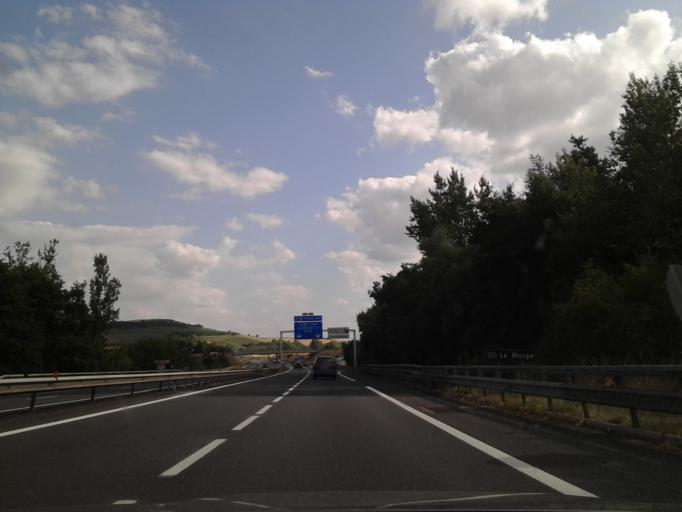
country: FR
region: Auvergne
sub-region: Departement du Puy-de-Dome
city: Combronde
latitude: 45.9996
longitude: 3.1093
